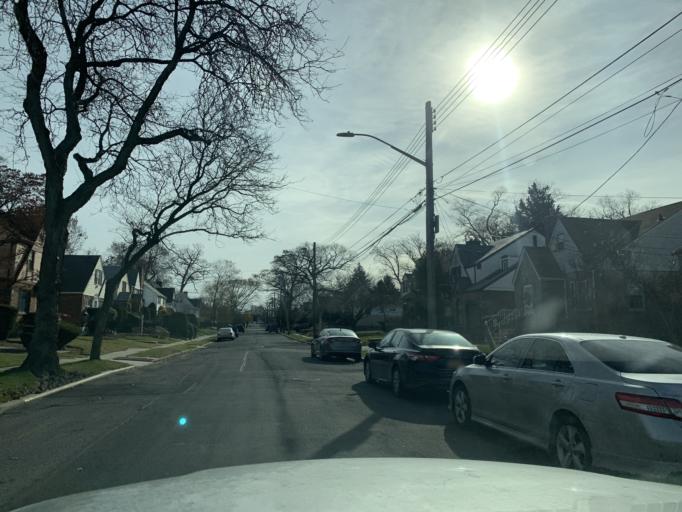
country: US
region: New York
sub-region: Queens County
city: Jamaica
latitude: 40.6958
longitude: -73.7747
